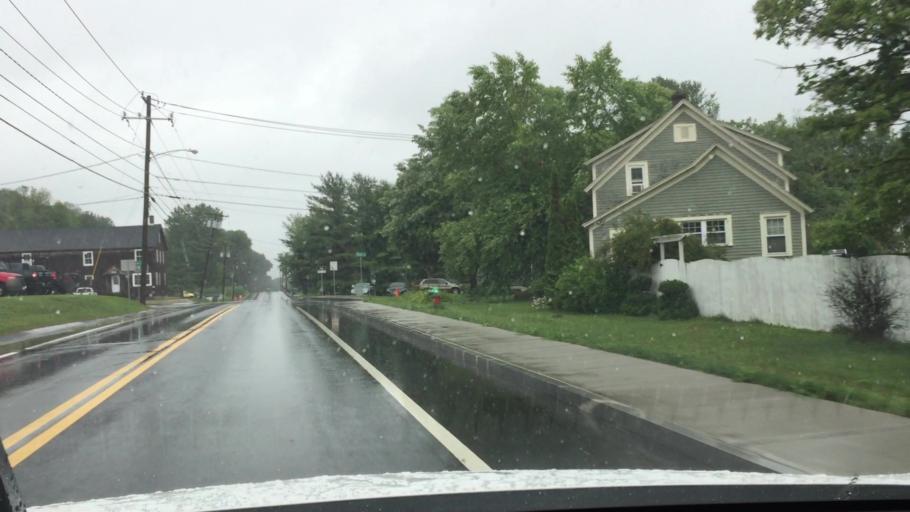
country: US
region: Massachusetts
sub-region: Berkshire County
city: Dalton
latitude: 42.4695
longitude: -73.1582
